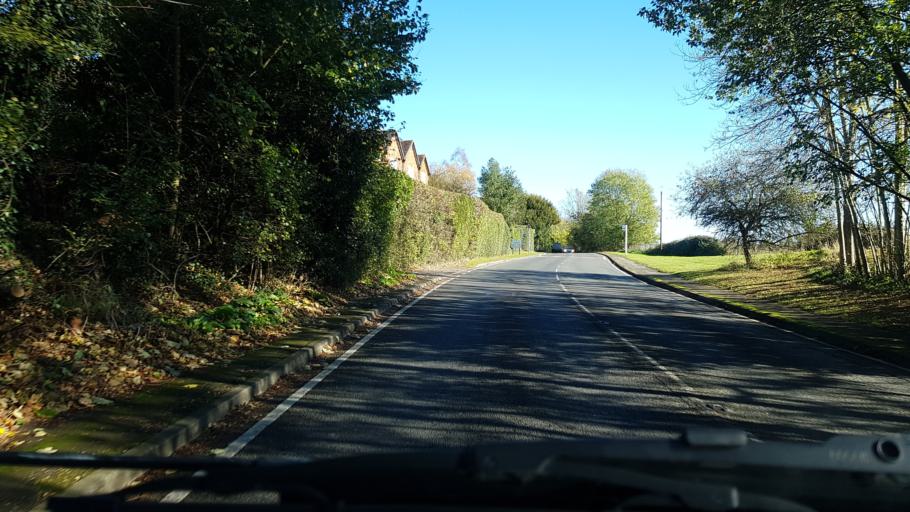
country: GB
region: England
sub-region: Surrey
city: Chilworth
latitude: 51.2209
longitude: -0.5060
